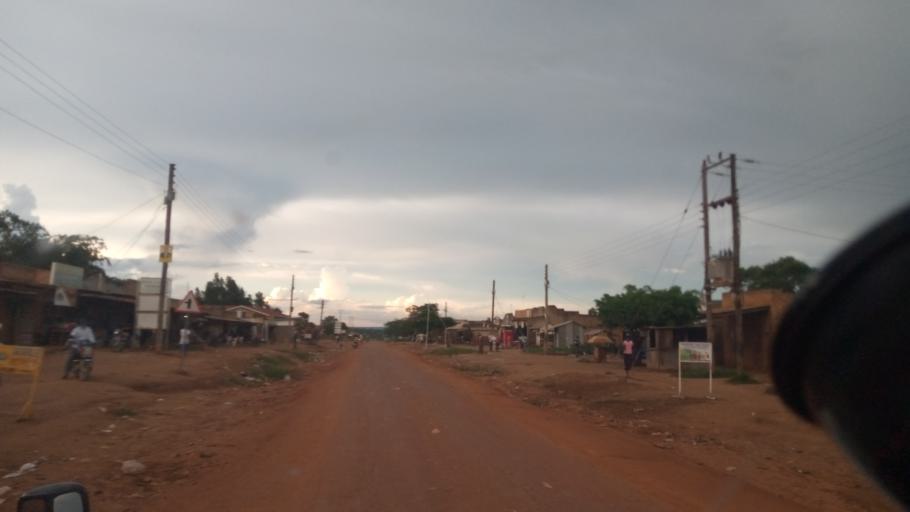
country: UG
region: Northern Region
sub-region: Kole District
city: Kole
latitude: 2.4864
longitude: 32.9353
